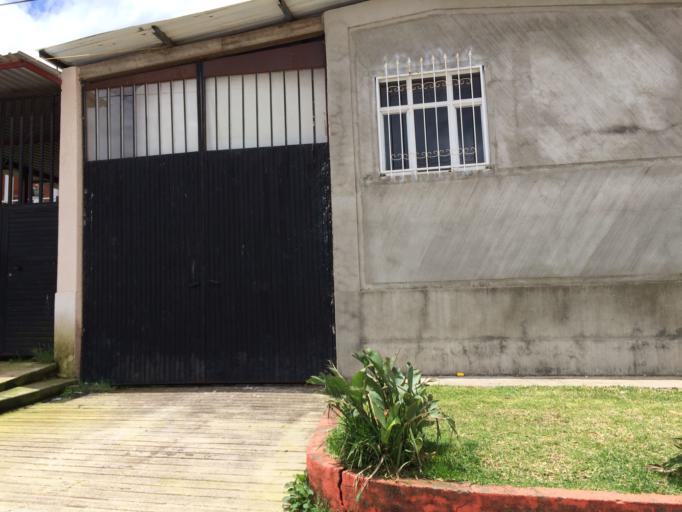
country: MX
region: Michoacan
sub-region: Uruapan
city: Nuevo Zirosto
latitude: 19.5471
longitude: -102.3461
